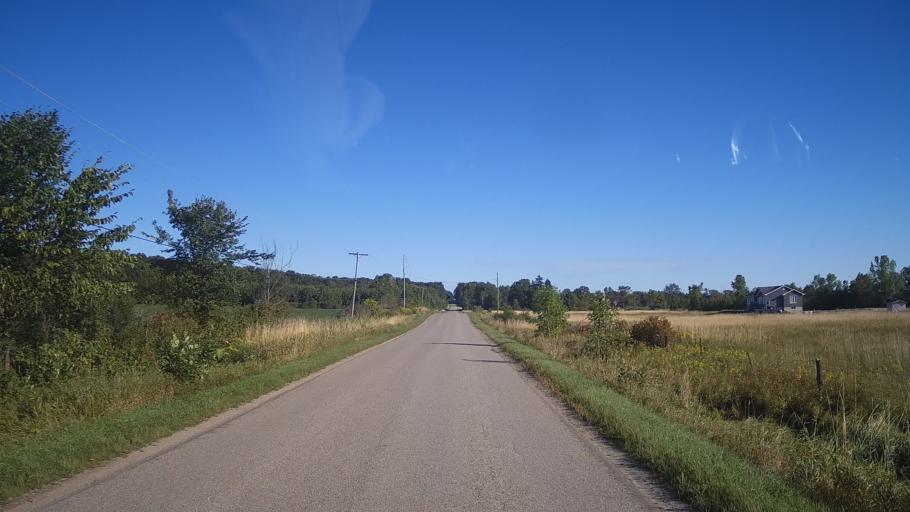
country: US
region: New York
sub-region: Jefferson County
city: Alexandria Bay
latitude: 44.4359
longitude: -75.9819
